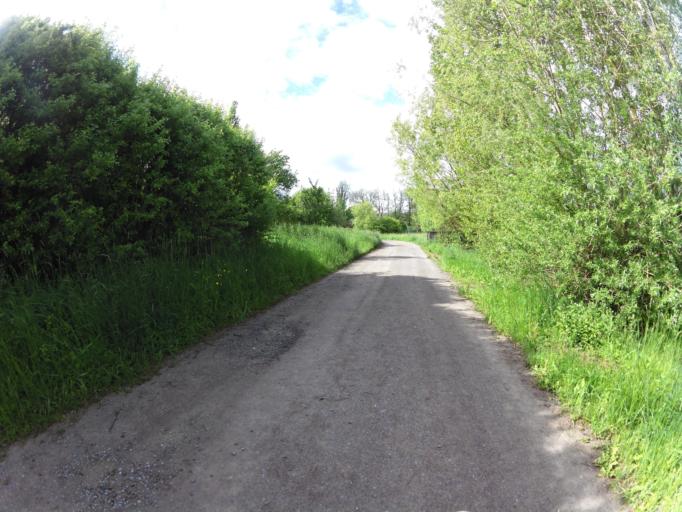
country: DE
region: Bavaria
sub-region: Regierungsbezirk Unterfranken
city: Volkach
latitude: 49.8668
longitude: 10.2348
